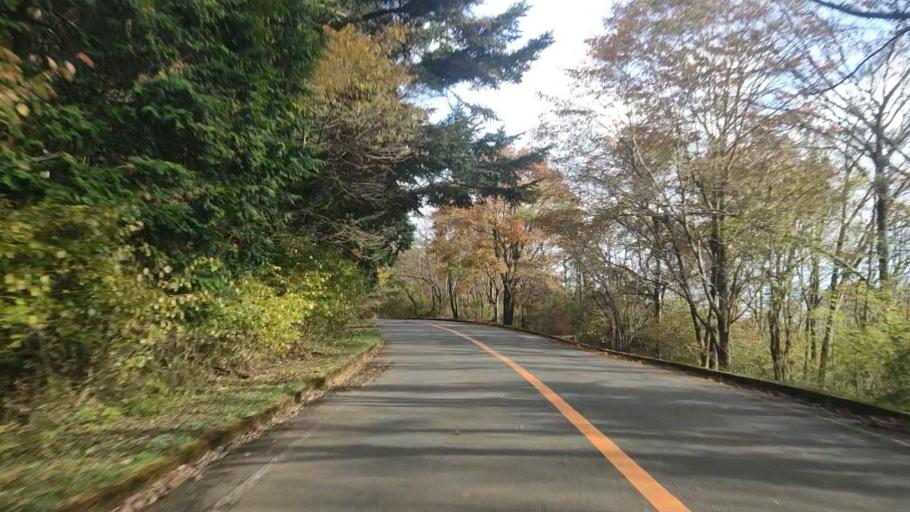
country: JP
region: Shizuoka
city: Fujinomiya
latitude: 35.3001
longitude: 138.6869
